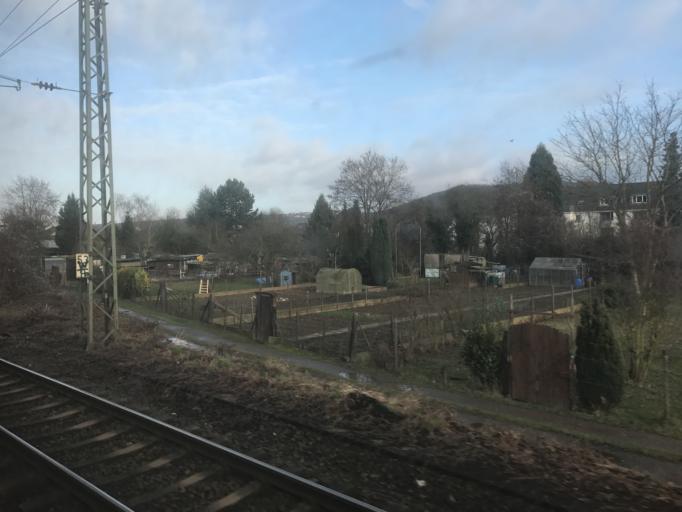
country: DE
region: Rheinland-Pfalz
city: Erpel
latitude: 50.5716
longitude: 7.2391
